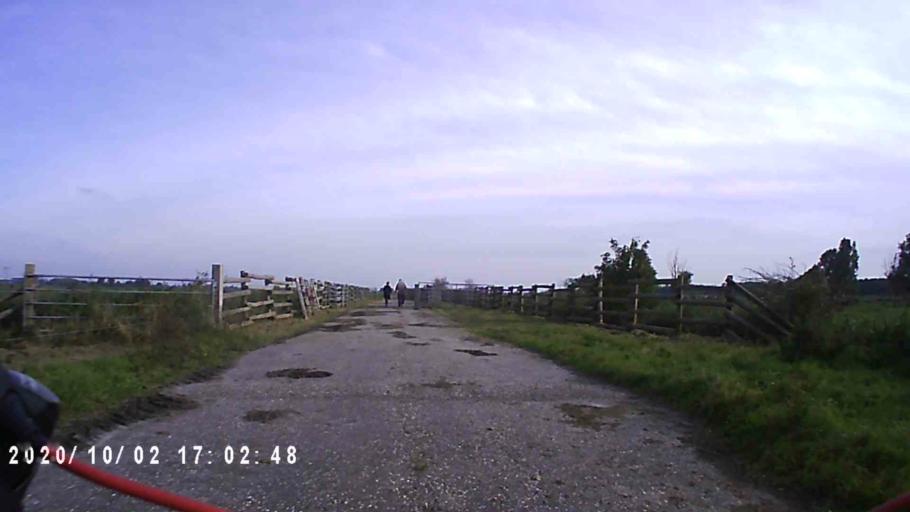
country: NL
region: Groningen
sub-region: Gemeente De Marne
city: Ulrum
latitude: 53.3426
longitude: 6.2623
